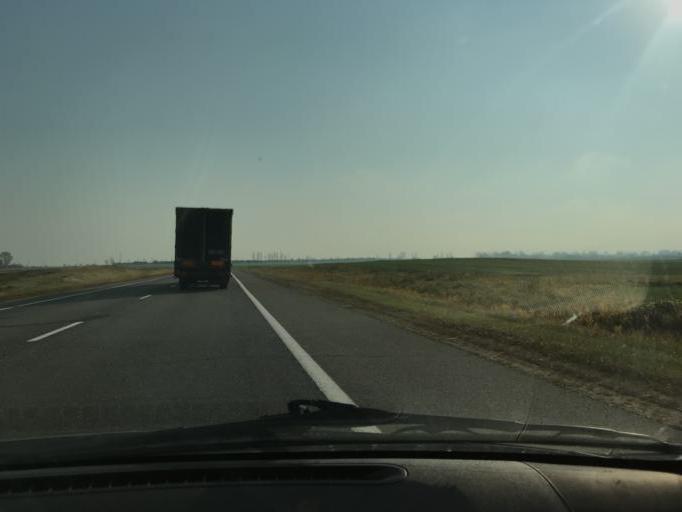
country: BY
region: Vitebsk
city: Chashniki
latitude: 55.0095
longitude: 29.1288
